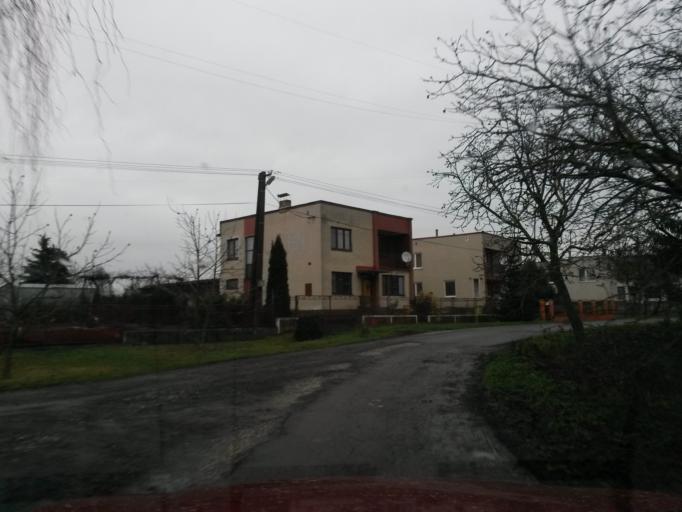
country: SK
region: Kosicky
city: Michalovce
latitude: 48.6633
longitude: 22.0290
